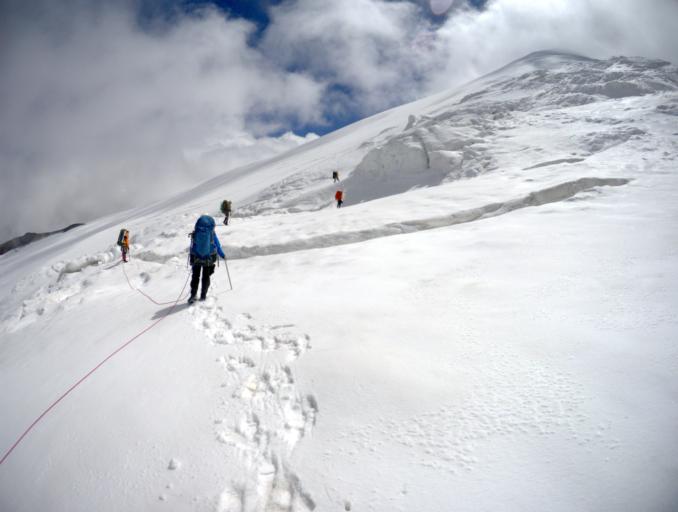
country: RU
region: Kabardino-Balkariya
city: Terskol
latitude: 43.3797
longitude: 42.4533
